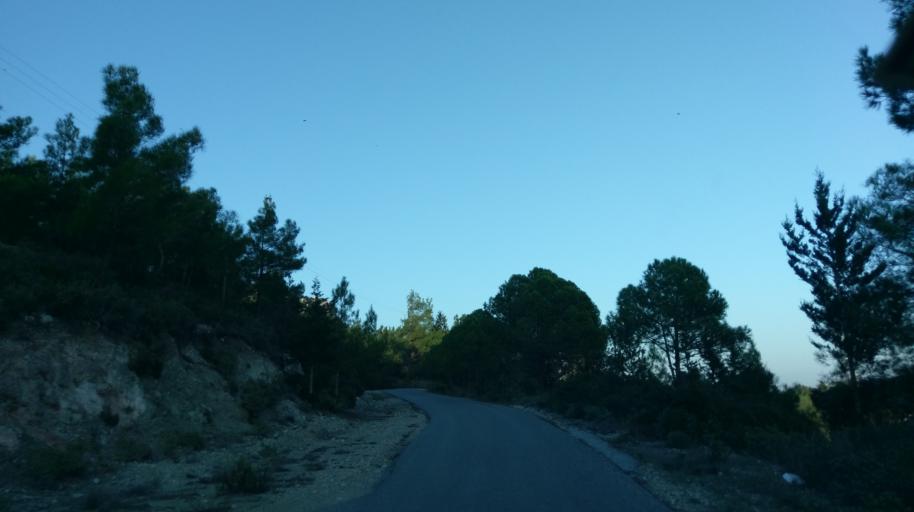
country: CY
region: Ammochostos
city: Trikomo
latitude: 35.3937
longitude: 33.9042
